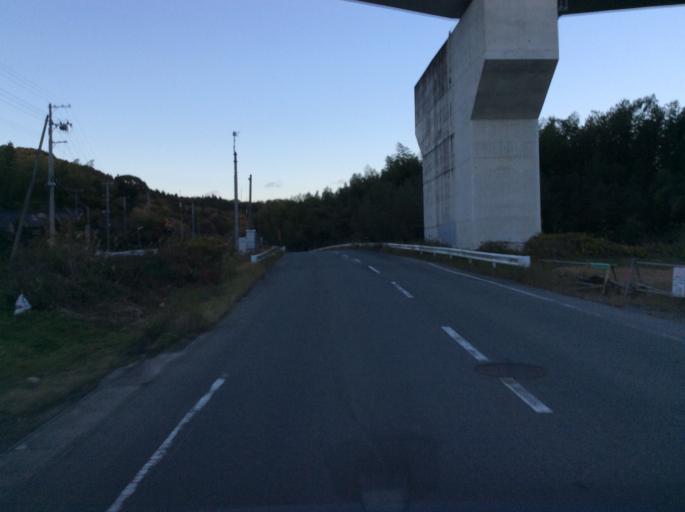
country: JP
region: Fukushima
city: Iwaki
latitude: 37.0960
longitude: 140.8599
